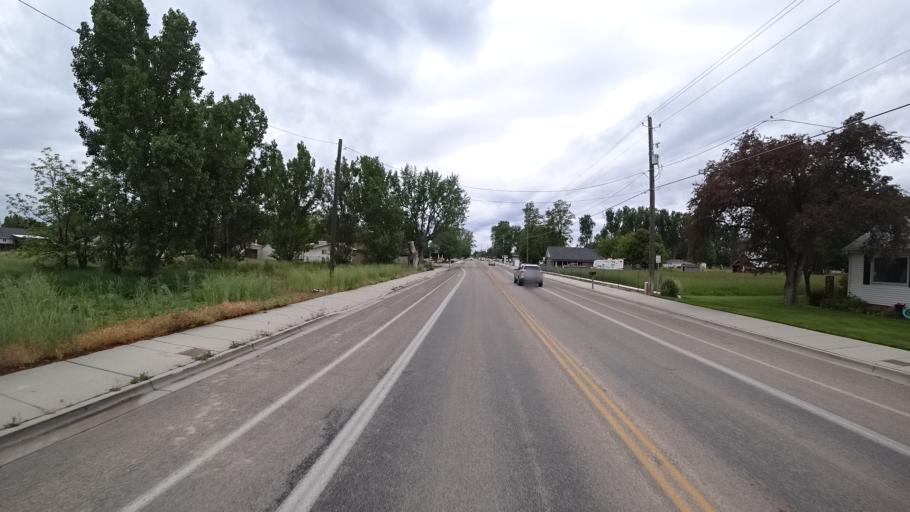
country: US
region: Idaho
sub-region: Ada County
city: Star
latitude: 43.6974
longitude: -116.4933
